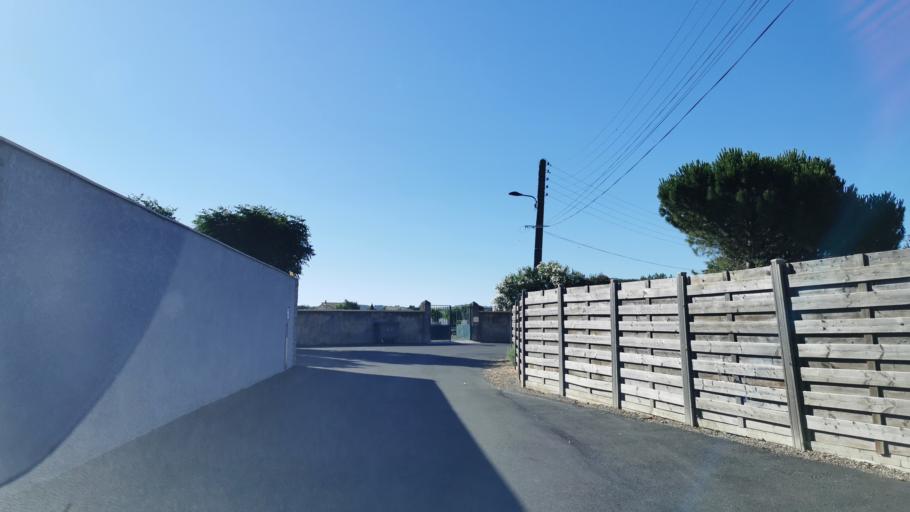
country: FR
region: Languedoc-Roussillon
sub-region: Departement de l'Aude
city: Coursan
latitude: 43.2356
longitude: 3.0673
